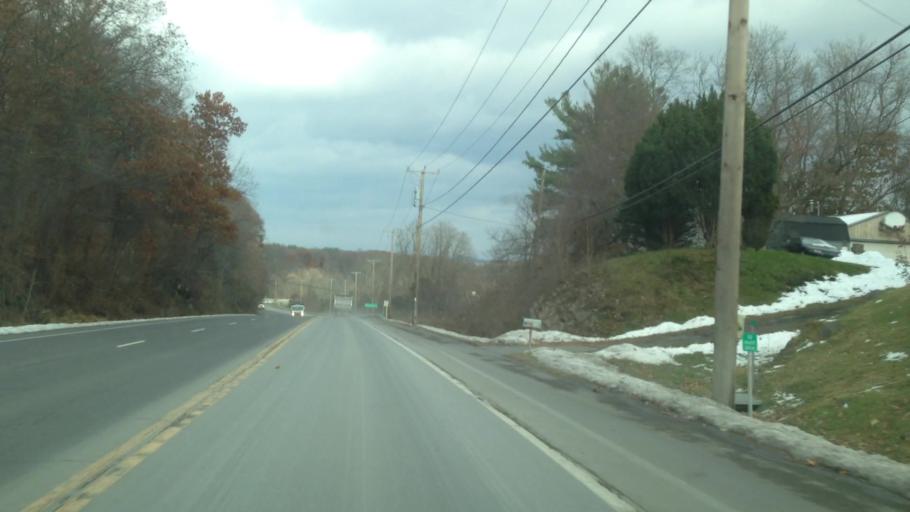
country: US
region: New York
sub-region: Ulster County
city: Lincoln Park
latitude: 41.9586
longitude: -73.9719
